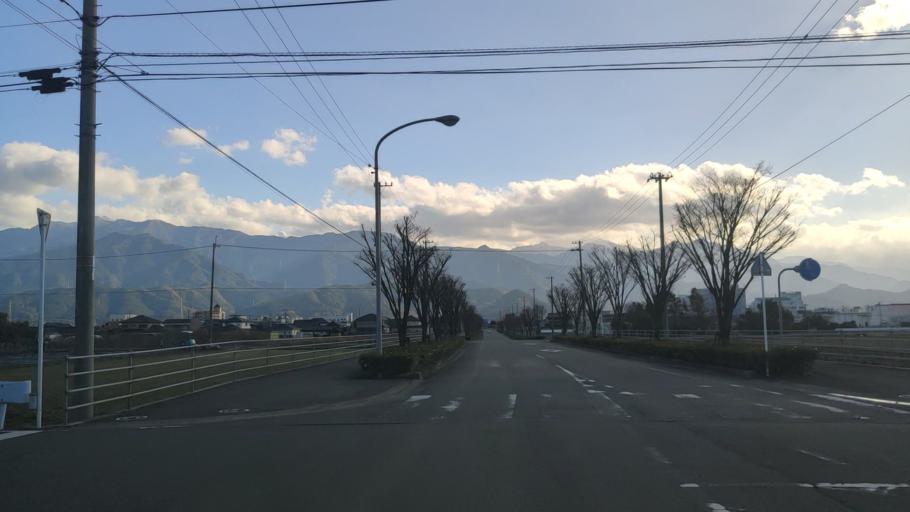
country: JP
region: Ehime
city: Saijo
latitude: 33.9345
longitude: 133.1926
